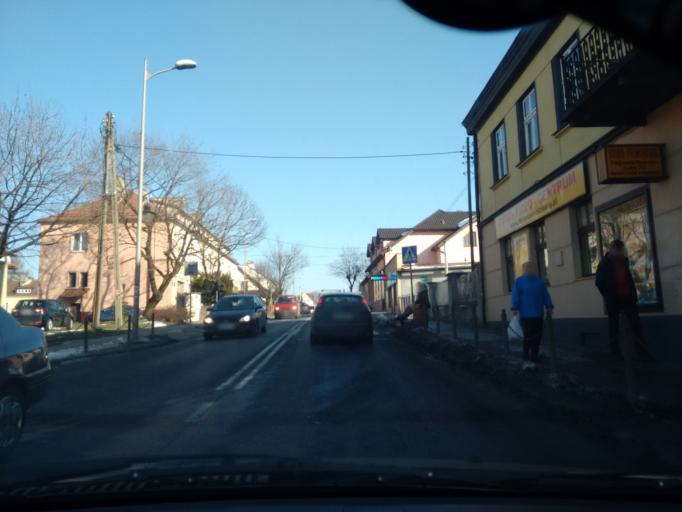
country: PL
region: Lesser Poland Voivodeship
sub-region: Powiat wadowicki
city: Andrychow
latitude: 49.8555
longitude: 19.3464
